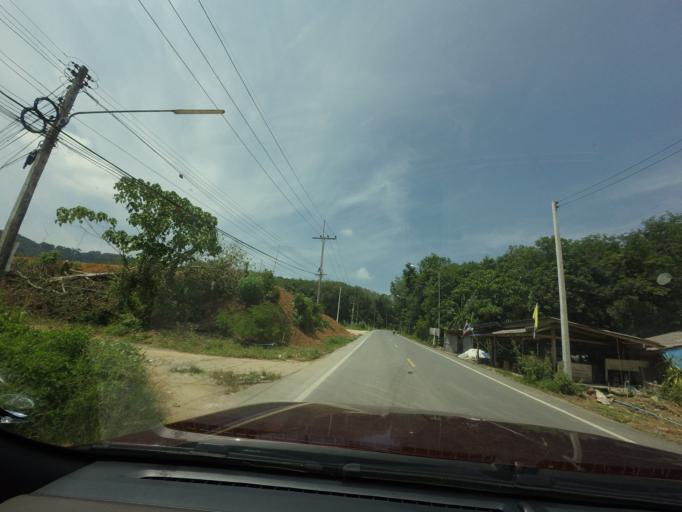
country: TH
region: Yala
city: Betong
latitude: 5.8475
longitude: 101.0744
